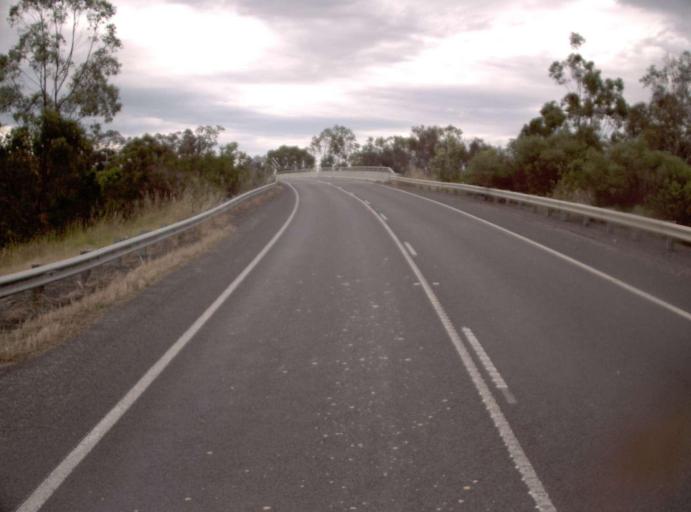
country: AU
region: Victoria
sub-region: Wellington
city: Sale
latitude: -38.1445
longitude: 147.0816
